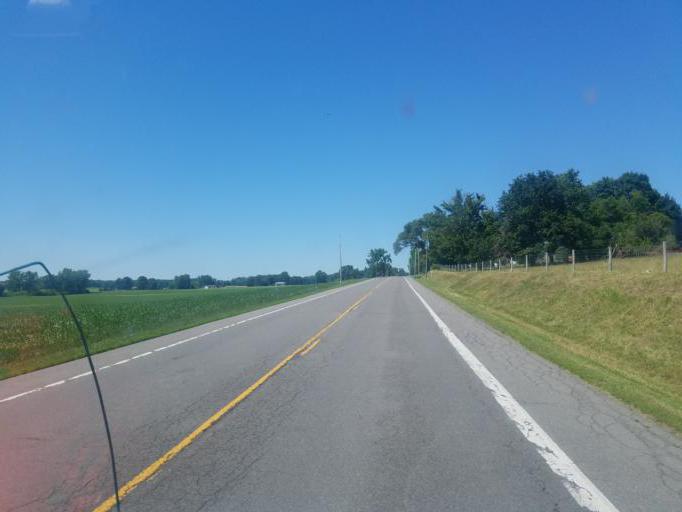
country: US
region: New York
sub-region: Ontario County
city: Geneva
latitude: 42.8344
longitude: -77.0374
